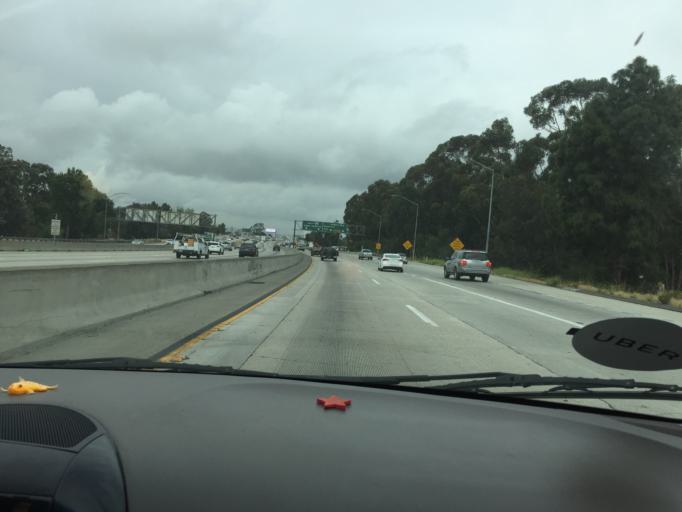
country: US
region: California
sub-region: Los Angeles County
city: Signal Hill
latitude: 33.8267
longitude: -118.2105
